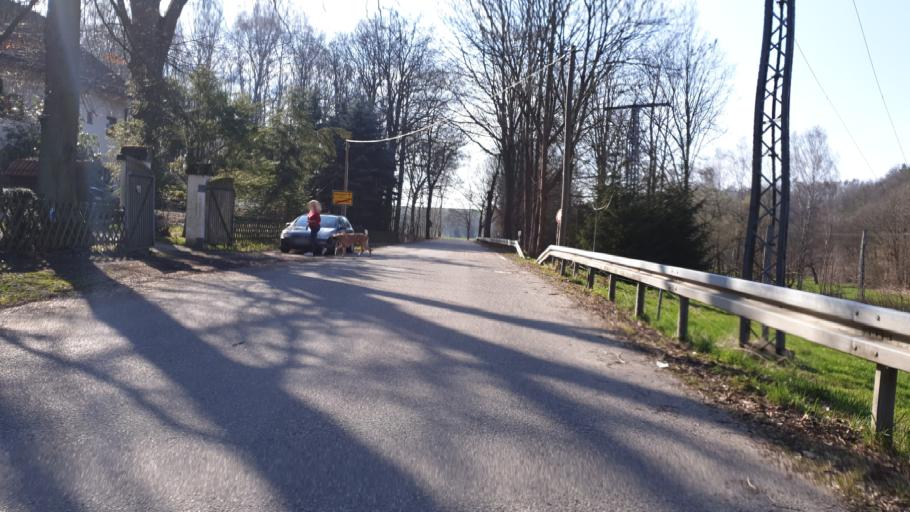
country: DE
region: Saxony
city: Taura
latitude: 50.9364
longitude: 12.8481
